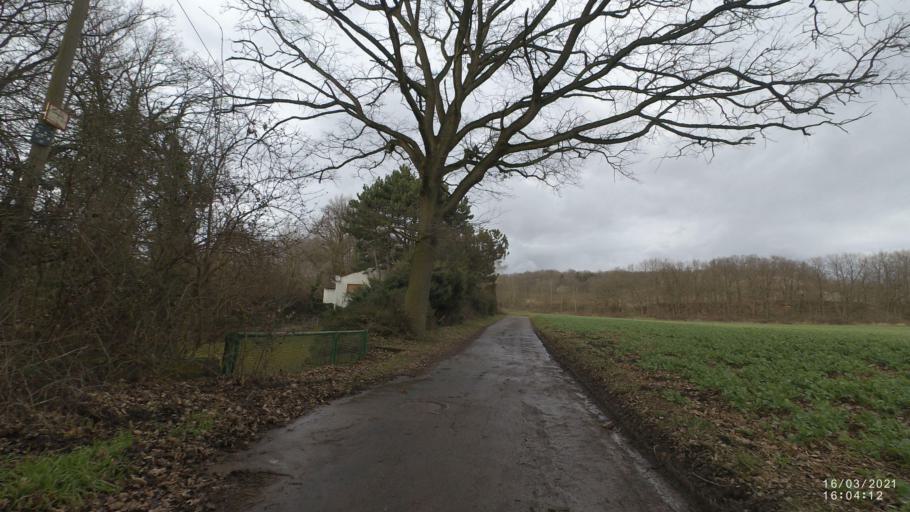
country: DE
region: Rheinland-Pfalz
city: Mendig
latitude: 50.3901
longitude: 7.2691
